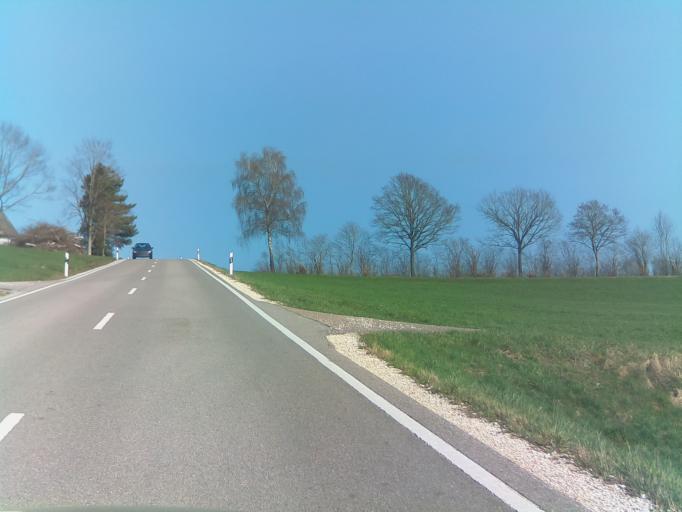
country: DE
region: Bavaria
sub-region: Swabia
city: Waltenhausen
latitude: 48.1878
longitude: 10.3447
